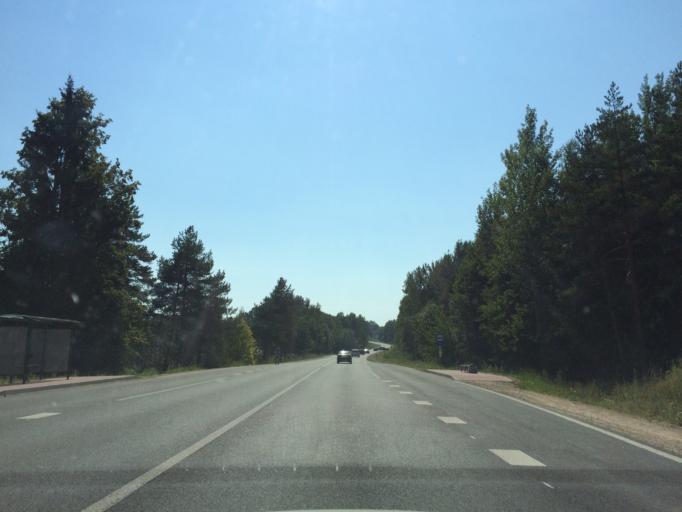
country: LV
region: Rezekne
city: Rezekne
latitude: 56.3680
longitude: 27.1855
